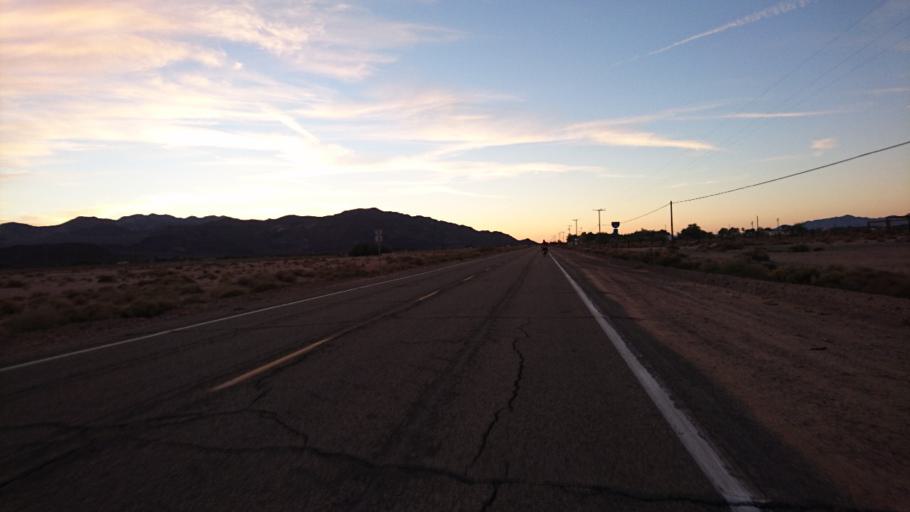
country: US
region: California
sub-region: San Bernardino County
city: Barstow
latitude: 34.8137
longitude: -116.6115
